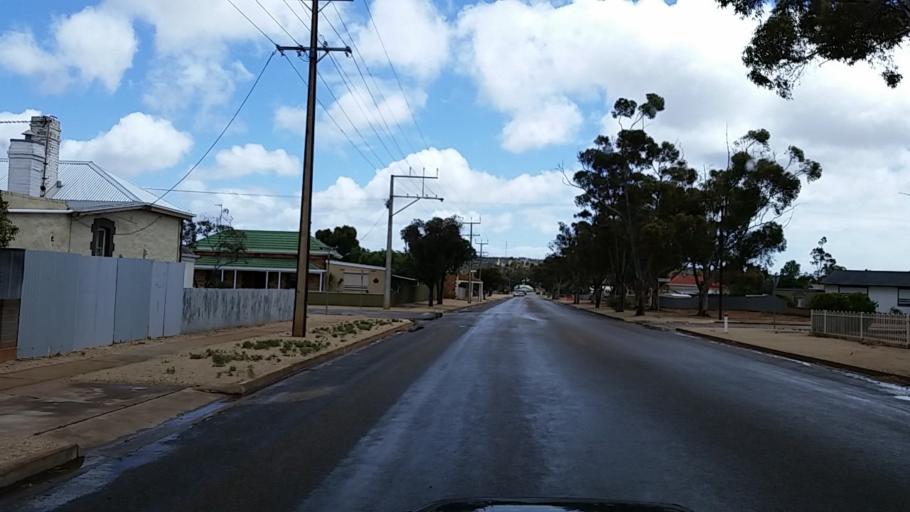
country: AU
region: South Australia
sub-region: Peterborough
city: Peterborough
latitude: -32.9778
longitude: 138.8318
